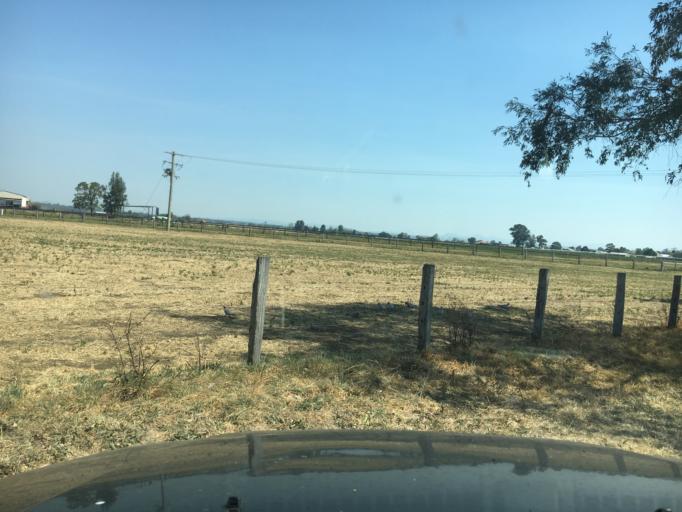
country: AU
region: New South Wales
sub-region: Singleton
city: Singleton
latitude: -32.5732
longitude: 151.1943
